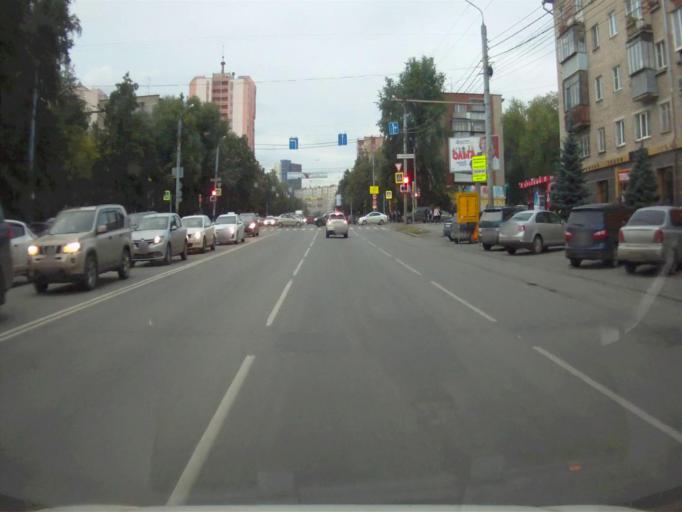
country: RU
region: Chelyabinsk
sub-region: Gorod Chelyabinsk
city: Chelyabinsk
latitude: 55.1589
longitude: 61.3809
